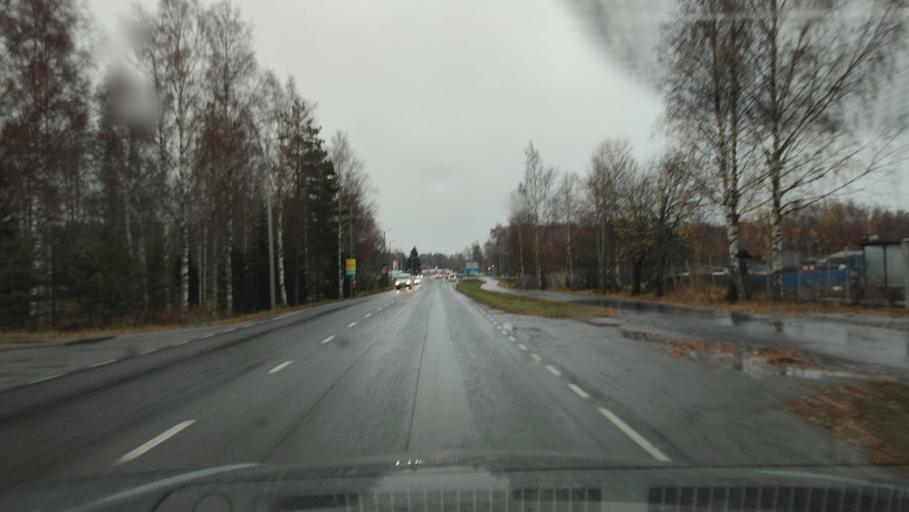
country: FI
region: Ostrobothnia
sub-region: Vaasa
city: Korsholm
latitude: 63.0916
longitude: 21.6536
